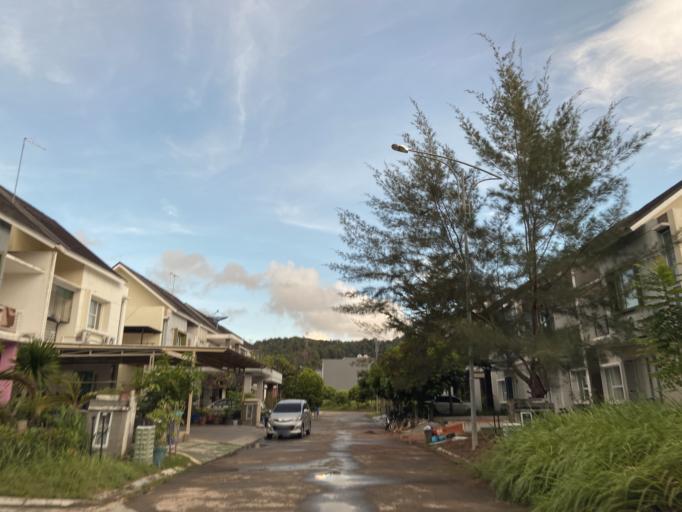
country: SG
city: Singapore
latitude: 1.0900
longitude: 104.0327
